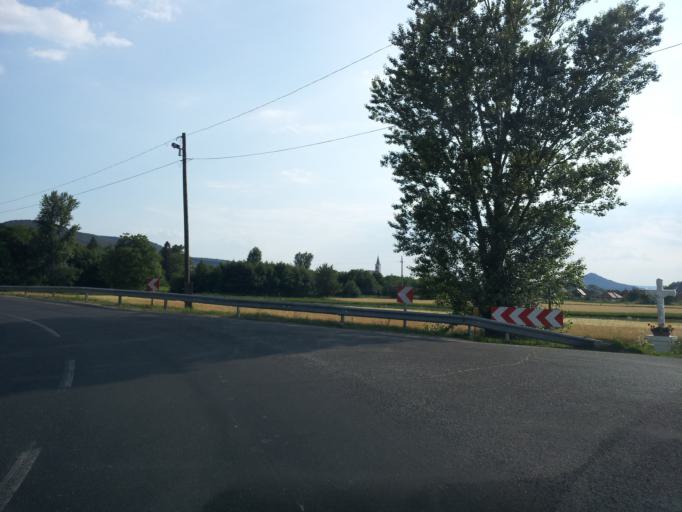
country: HU
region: Veszprem
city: Revfueloep
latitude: 46.9287
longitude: 17.5595
